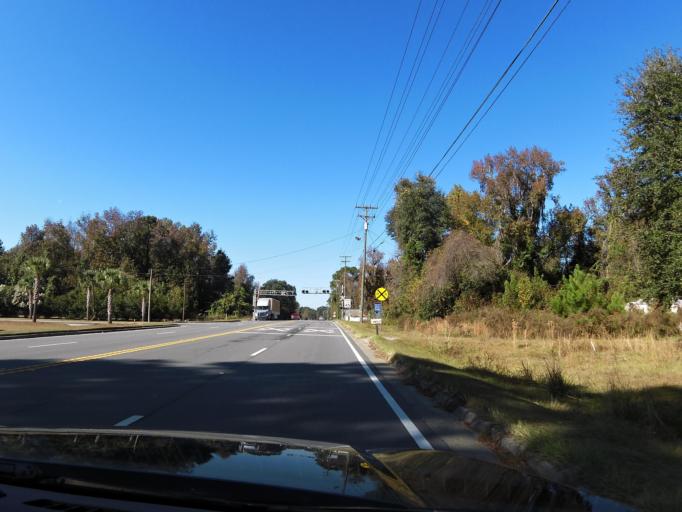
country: US
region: Georgia
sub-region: Liberty County
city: Midway
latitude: 31.7948
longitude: -81.4043
